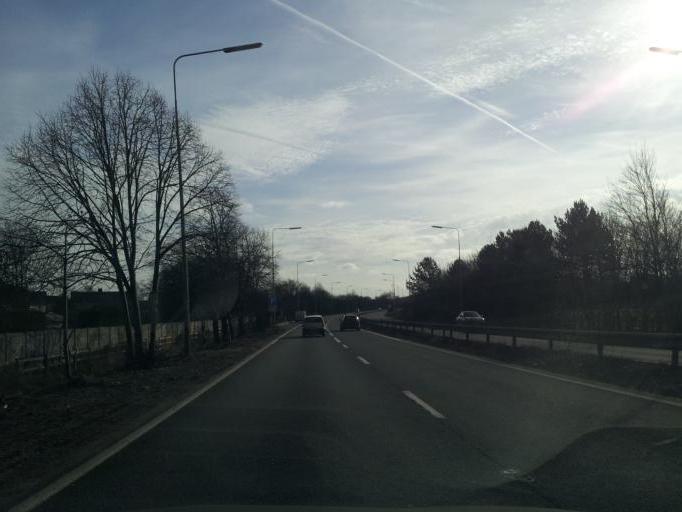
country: GB
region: England
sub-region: Central Bedfordshire
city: Biggleswade
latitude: 52.0770
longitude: -0.2572
